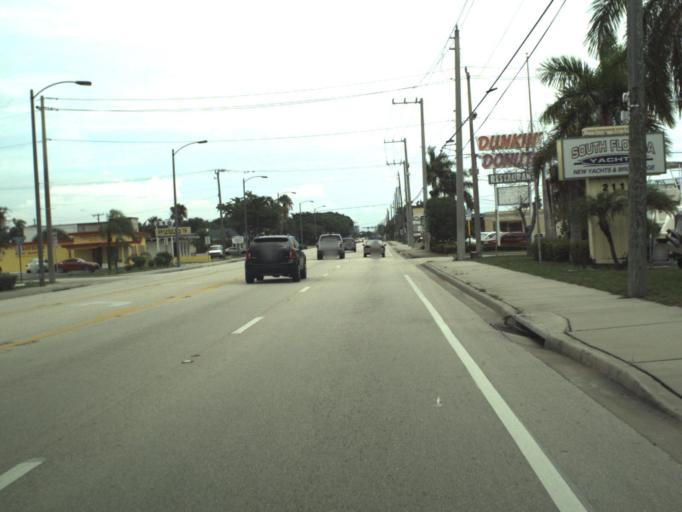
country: US
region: Florida
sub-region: Palm Beach County
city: Lake Park
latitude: 26.7939
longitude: -80.0542
